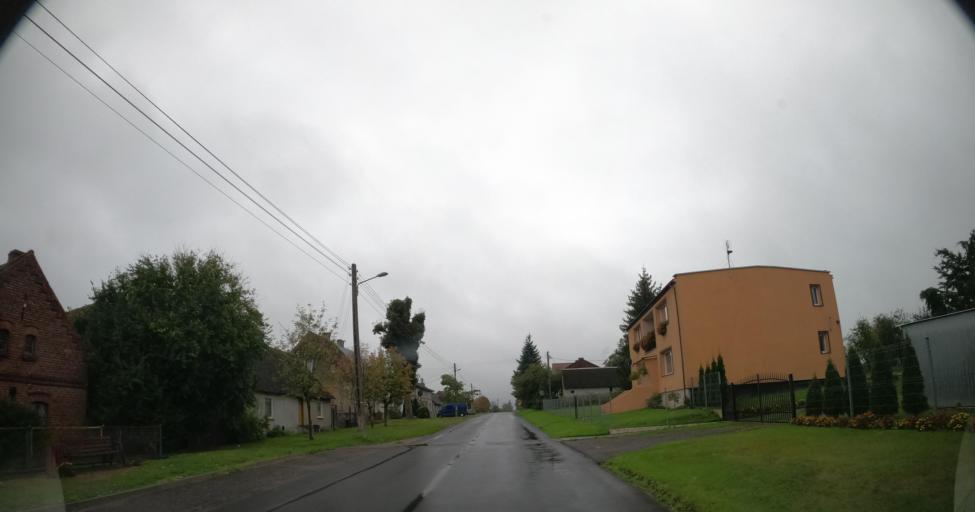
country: PL
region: West Pomeranian Voivodeship
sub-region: Powiat pyrzycki
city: Kozielice
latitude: 53.0481
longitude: 14.7739
